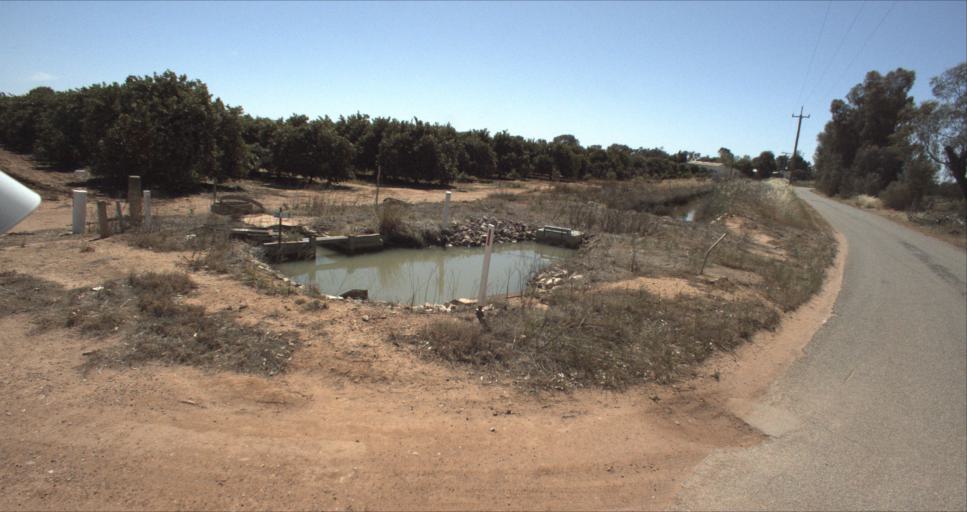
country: AU
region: New South Wales
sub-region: Leeton
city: Leeton
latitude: -34.5292
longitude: 146.3460
